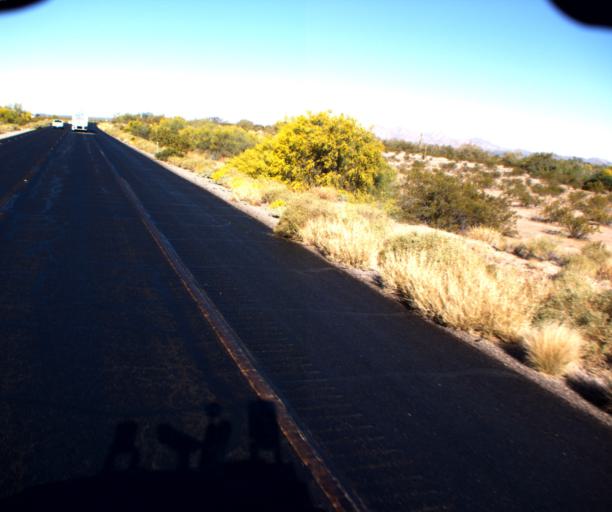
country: US
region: Arizona
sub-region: Pinal County
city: Maricopa
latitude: 32.8367
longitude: -112.2068
